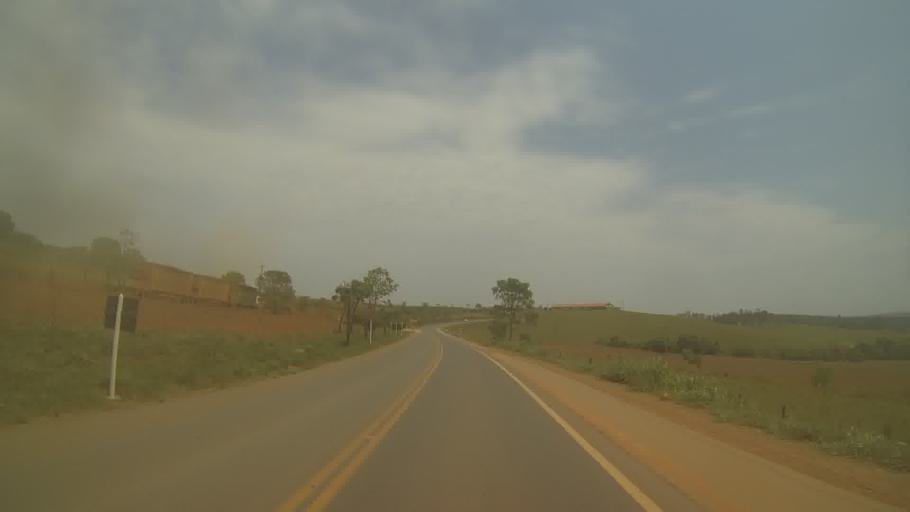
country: BR
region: Minas Gerais
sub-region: Bambui
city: Bambui
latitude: -20.0152
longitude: -45.9373
